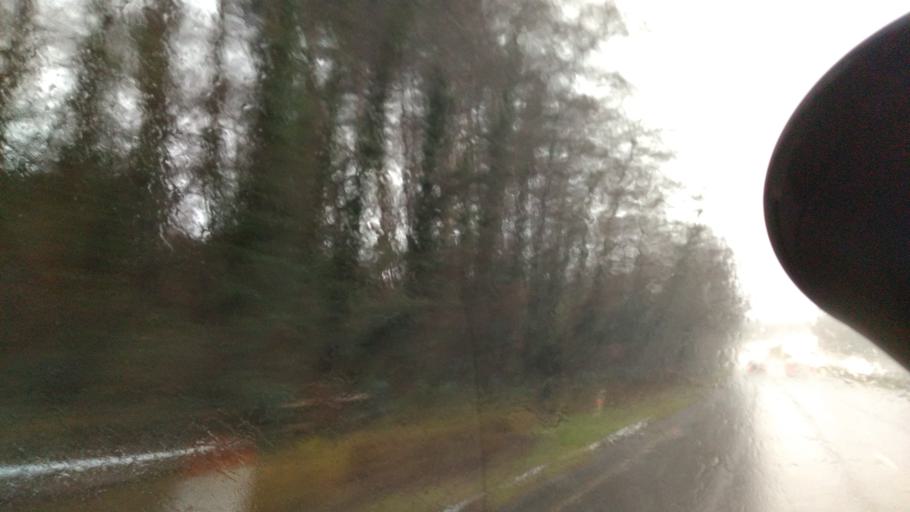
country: GB
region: England
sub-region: West Sussex
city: Walberton
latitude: 50.8543
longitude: -0.6117
